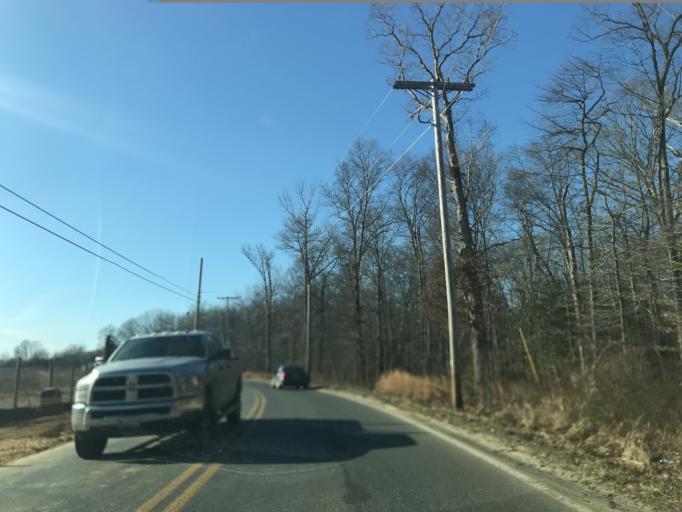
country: US
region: Maryland
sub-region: Charles County
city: Waldorf
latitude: 38.6740
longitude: -76.9662
